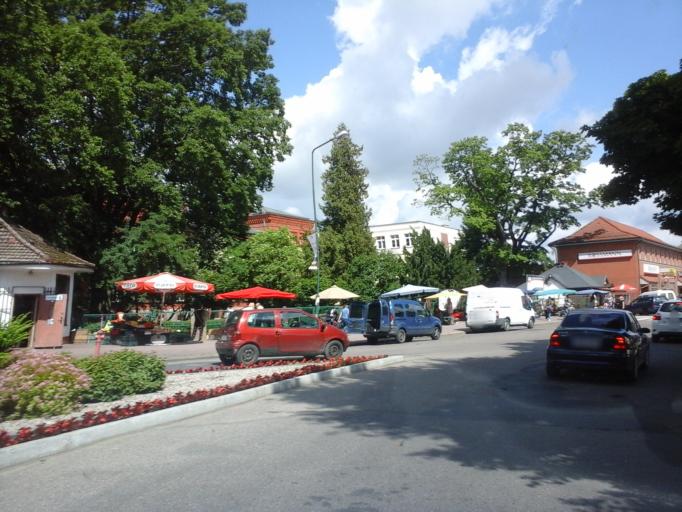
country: PL
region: West Pomeranian Voivodeship
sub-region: Powiat swidwinski
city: Swidwin
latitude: 53.7759
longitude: 15.7736
